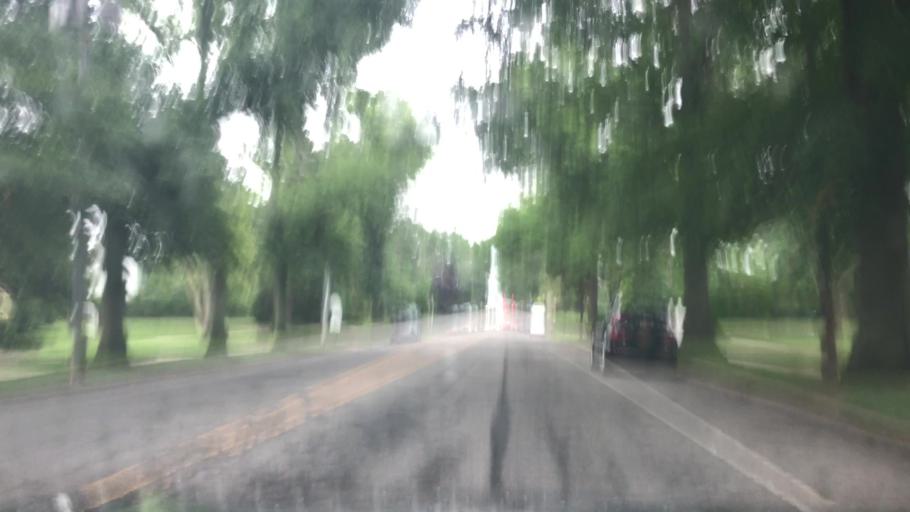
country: US
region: New York
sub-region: Nassau County
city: West Hempstead
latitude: 40.7100
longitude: -73.6353
